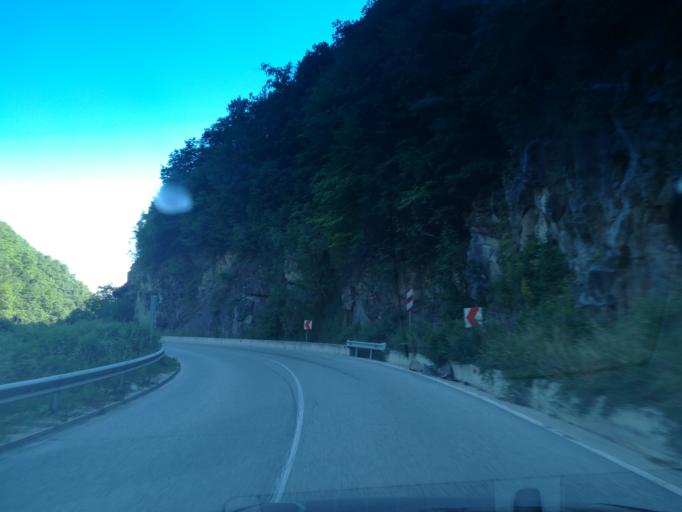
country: BG
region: Smolyan
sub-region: Obshtina Chepelare
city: Chepelare
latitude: 41.7860
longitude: 24.7085
